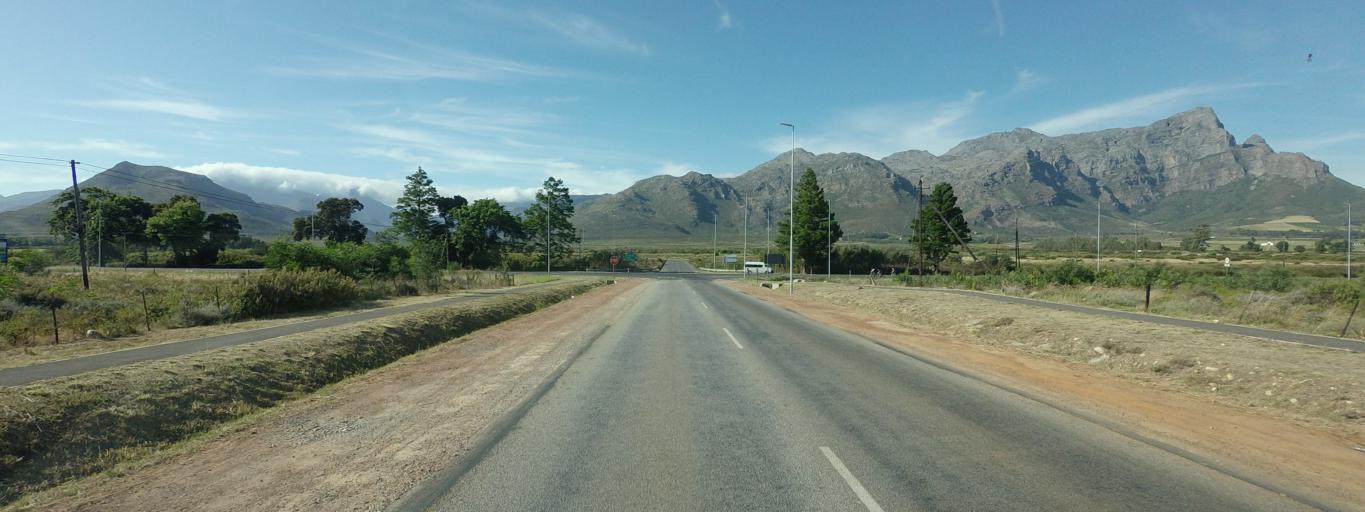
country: ZA
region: Western Cape
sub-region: Cape Winelands District Municipality
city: Paarl
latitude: -33.8772
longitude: 19.0445
